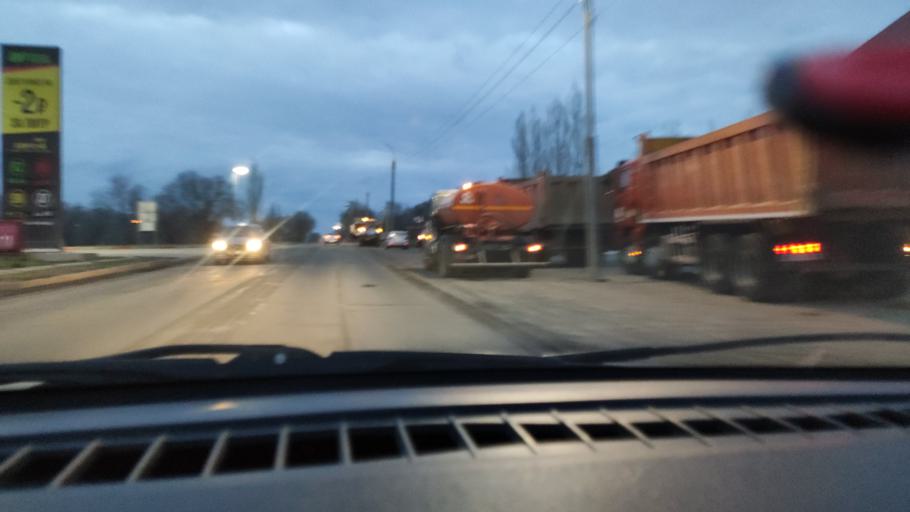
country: RU
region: Orenburg
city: Tatarskaya Kargala
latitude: 51.8704
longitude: 55.1439
